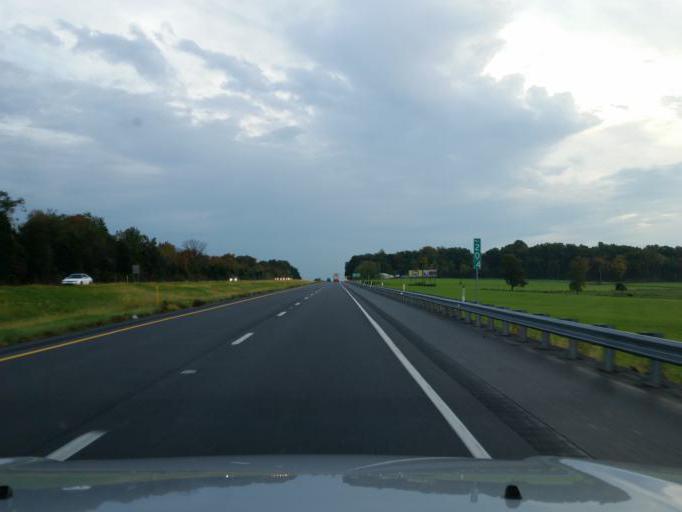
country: US
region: Pennsylvania
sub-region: Adams County
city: Lake Meade
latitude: 39.9595
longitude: -77.1313
